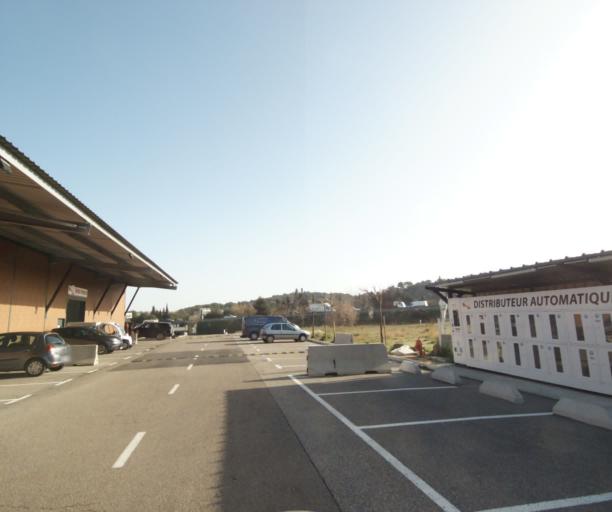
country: FR
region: Provence-Alpes-Cote d'Azur
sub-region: Departement des Bouches-du-Rhone
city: Septemes-les-Vallons
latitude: 43.4115
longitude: 5.3631
